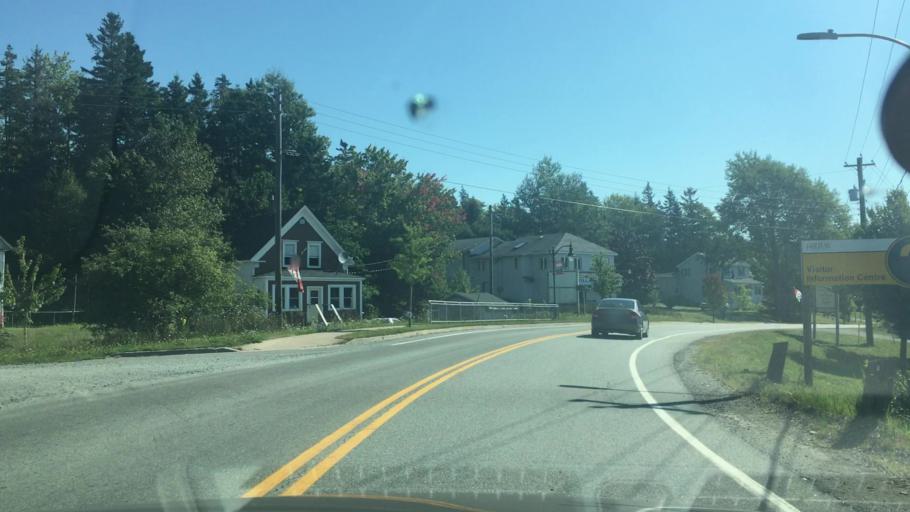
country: CA
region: Nova Scotia
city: New Glasgow
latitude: 44.9279
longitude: -62.5443
